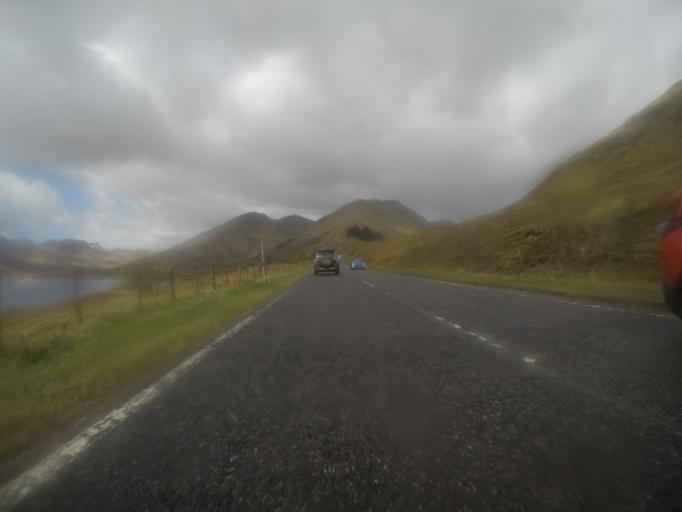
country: GB
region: Scotland
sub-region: Highland
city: Fort William
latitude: 57.1580
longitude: -5.1522
